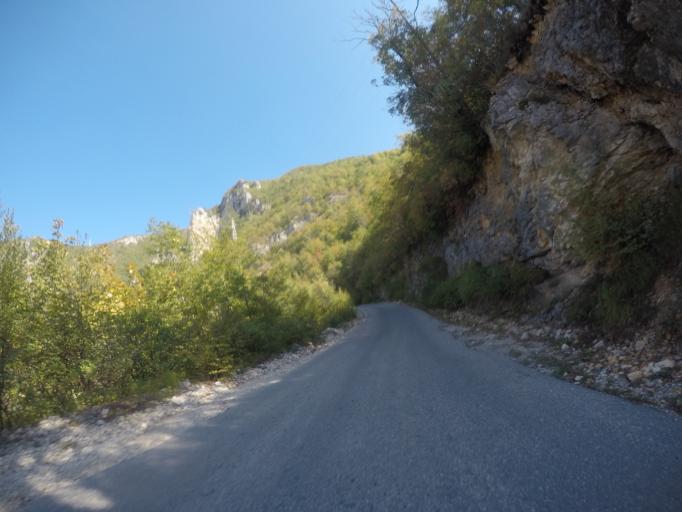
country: ME
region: Opstina Pluzine
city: Pluzine
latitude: 43.1697
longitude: 18.8612
